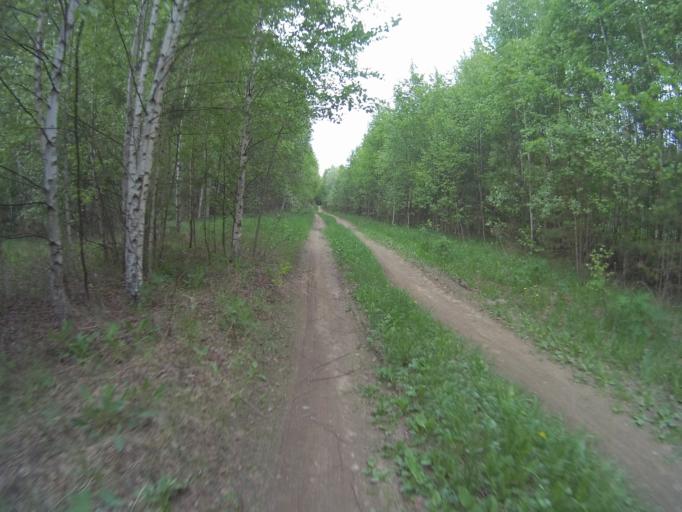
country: RU
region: Vladimir
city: Raduzhnyy
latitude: 56.0192
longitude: 40.2320
